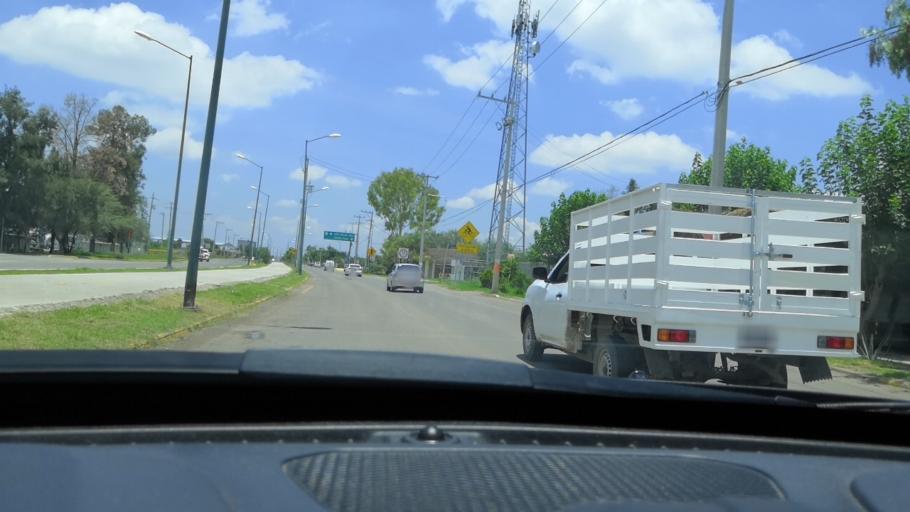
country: MX
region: Guanajuato
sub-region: Silao de la Victoria
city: El Refugio de los Sauces
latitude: 21.0227
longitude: -101.5779
